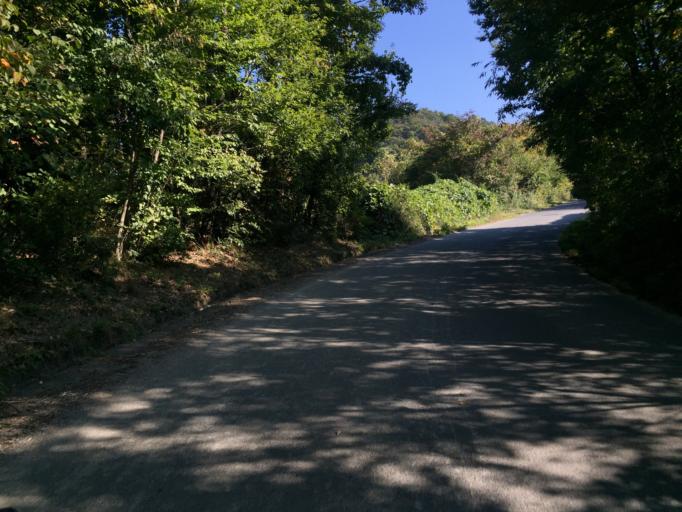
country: JP
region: Fukushima
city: Fukushima-shi
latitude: 37.7073
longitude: 140.4576
